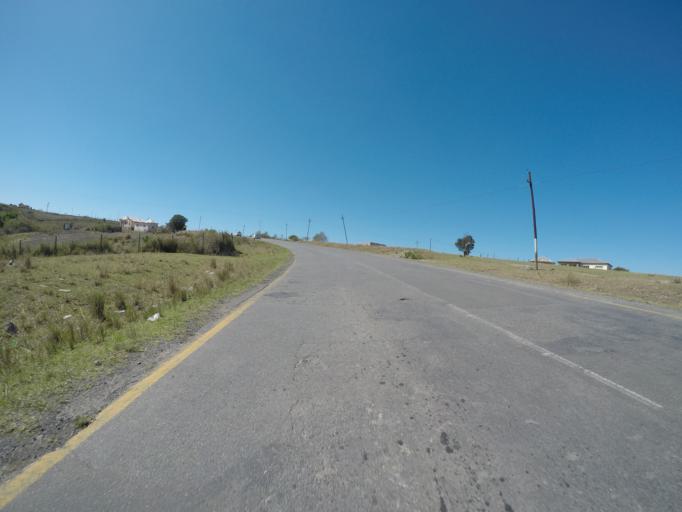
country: ZA
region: Eastern Cape
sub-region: OR Tambo District Municipality
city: Mthatha
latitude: -31.9201
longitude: 28.9676
